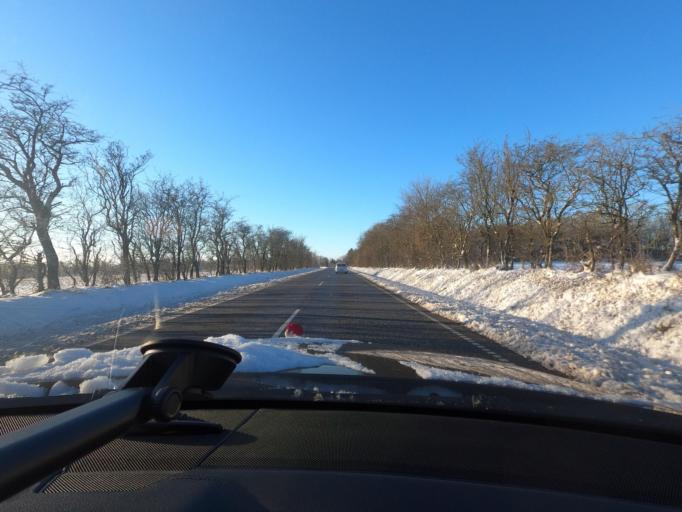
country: DK
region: South Denmark
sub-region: Tonder Kommune
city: Logumkloster
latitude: 55.1799
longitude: 8.9095
